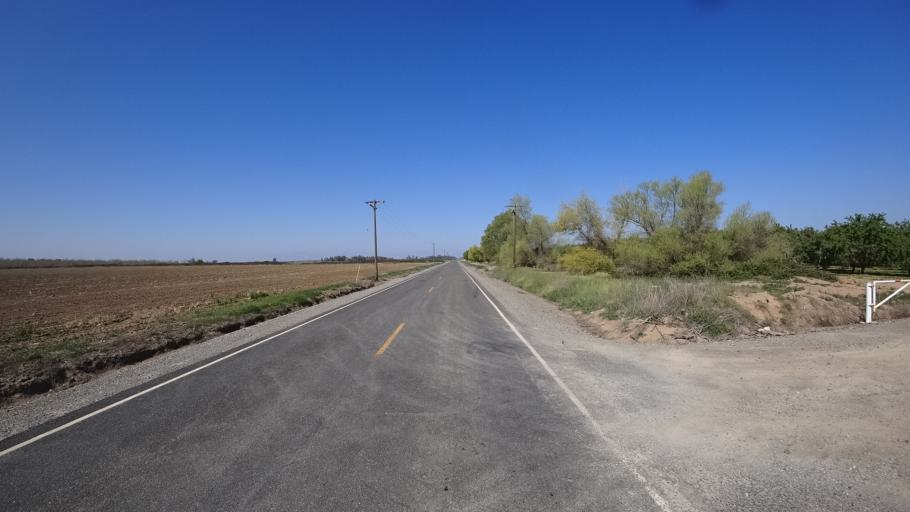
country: US
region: California
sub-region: Glenn County
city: Hamilton City
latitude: 39.6597
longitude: -122.0306
